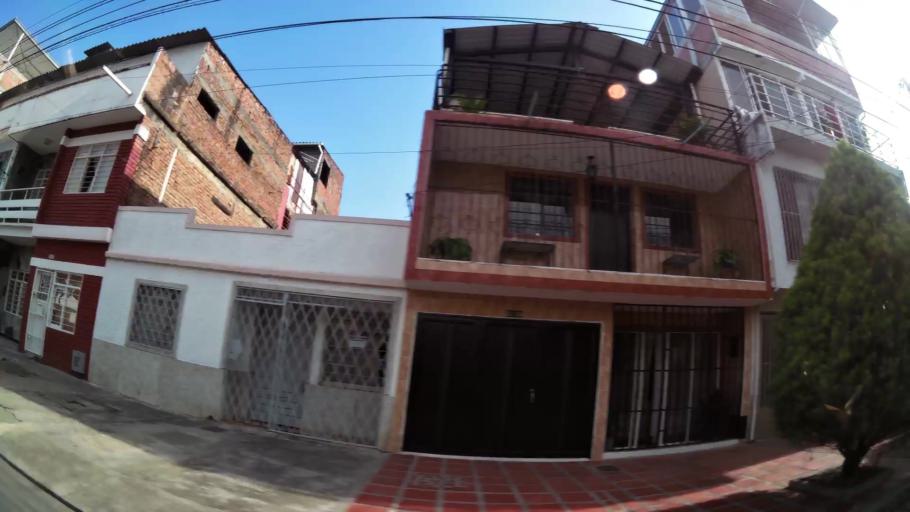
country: CO
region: Valle del Cauca
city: Cali
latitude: 3.4268
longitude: -76.5259
